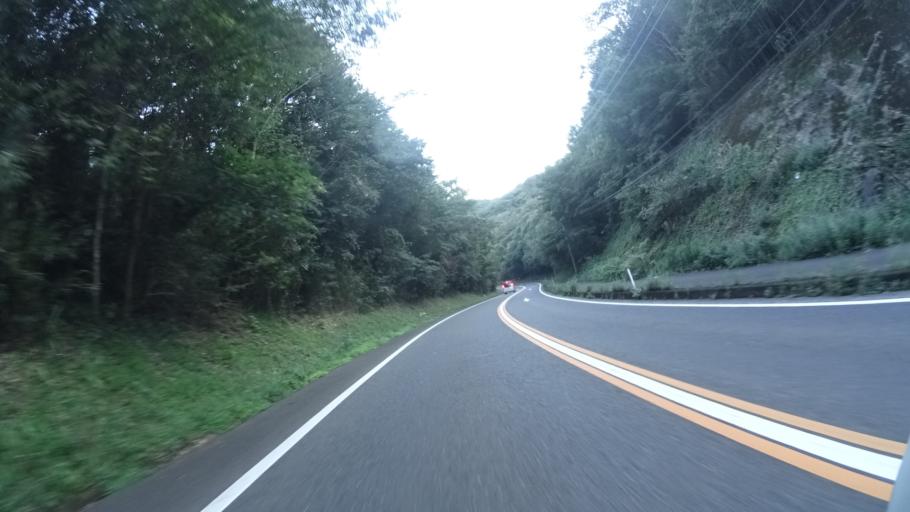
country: JP
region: Oita
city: Hiji
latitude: 33.3501
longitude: 131.4517
